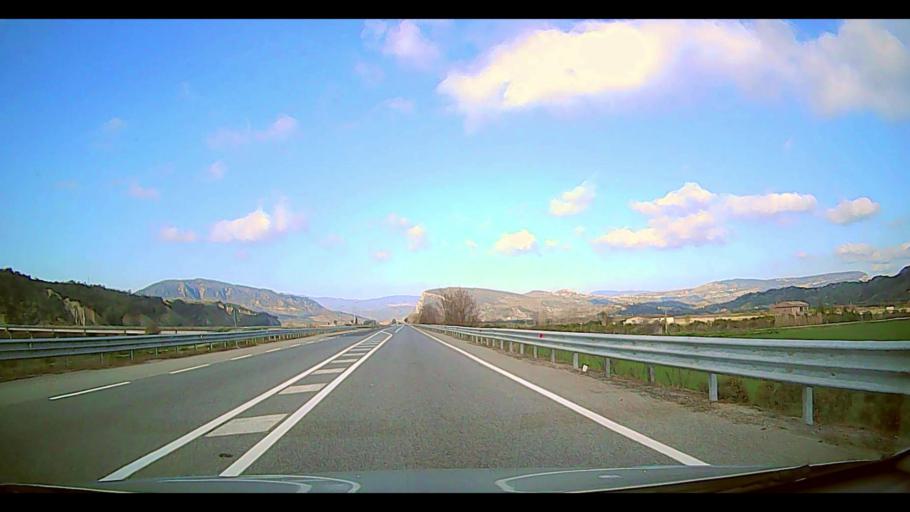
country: IT
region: Calabria
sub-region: Provincia di Crotone
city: Santa Severina
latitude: 39.1748
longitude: 16.9349
